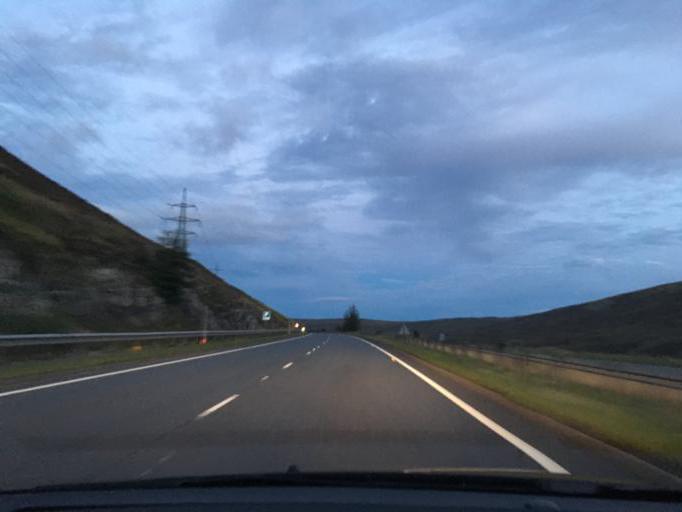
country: GB
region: Scotland
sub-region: Highland
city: Kingussie
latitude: 56.8294
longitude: -4.2156
